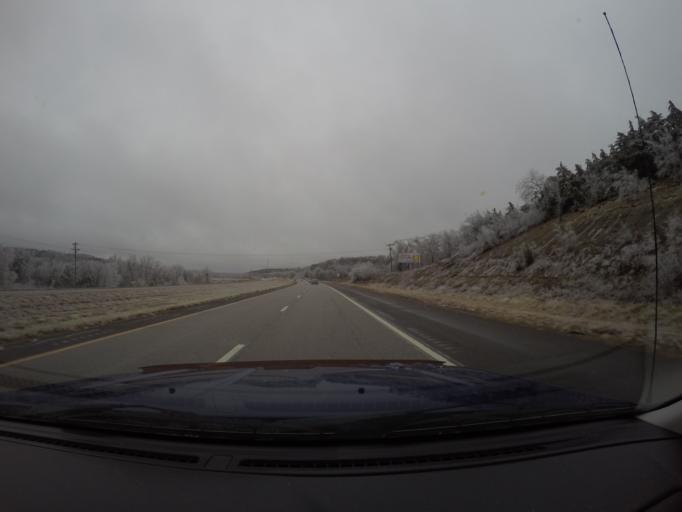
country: US
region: Kansas
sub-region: Riley County
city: Manhattan
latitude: 39.1586
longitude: -96.5383
